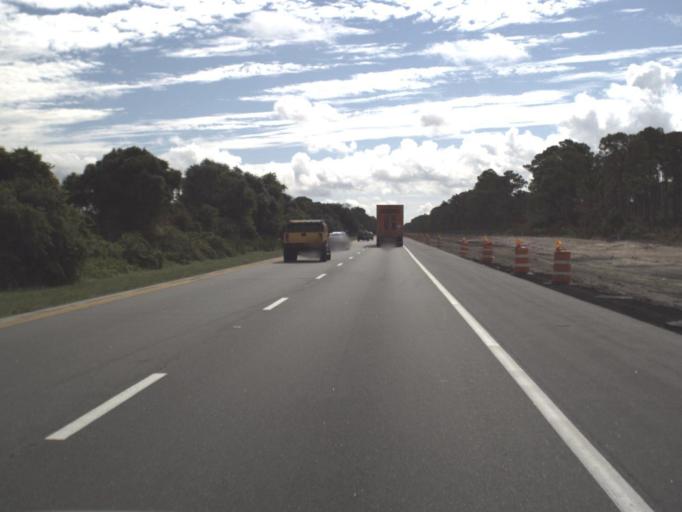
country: US
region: Florida
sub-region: Sarasota County
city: Warm Mineral Springs
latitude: 27.0998
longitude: -82.2685
